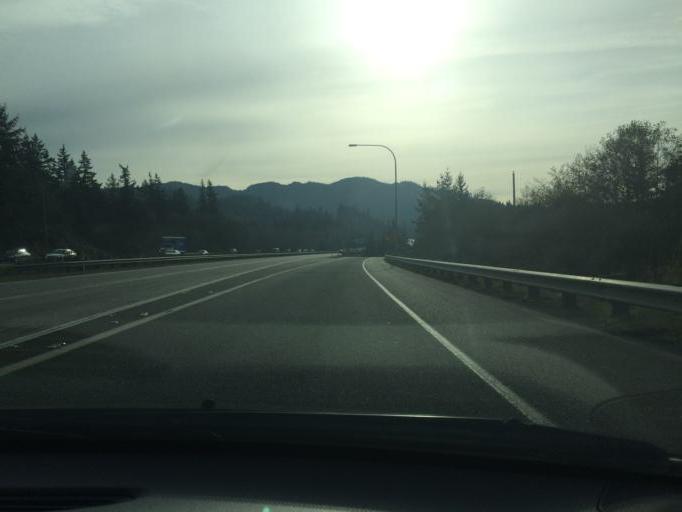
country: US
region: Washington
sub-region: Whatcom County
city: Bellingham
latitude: 48.7172
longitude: -122.4740
